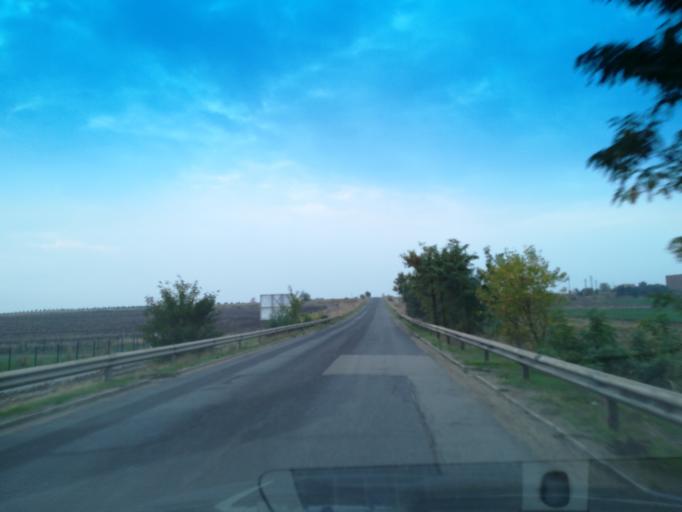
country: BG
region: Stara Zagora
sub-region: Obshtina Chirpan
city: Chirpan
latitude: 42.1914
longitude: 25.3177
